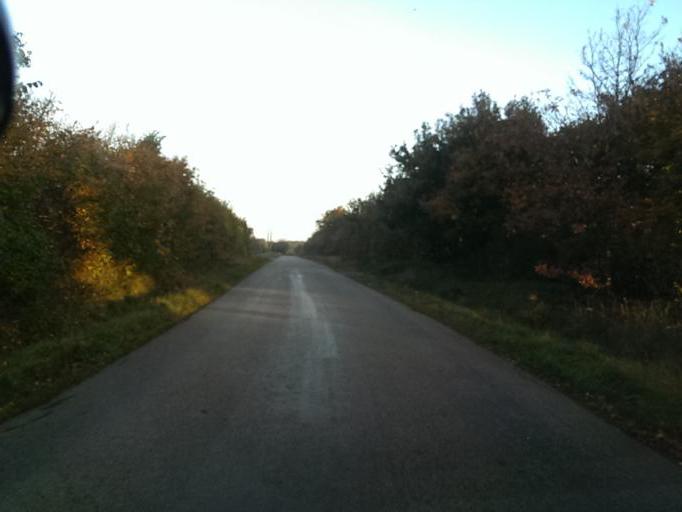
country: DK
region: South Denmark
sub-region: Esbjerg Kommune
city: Tjaereborg
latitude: 55.4713
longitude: 8.6316
